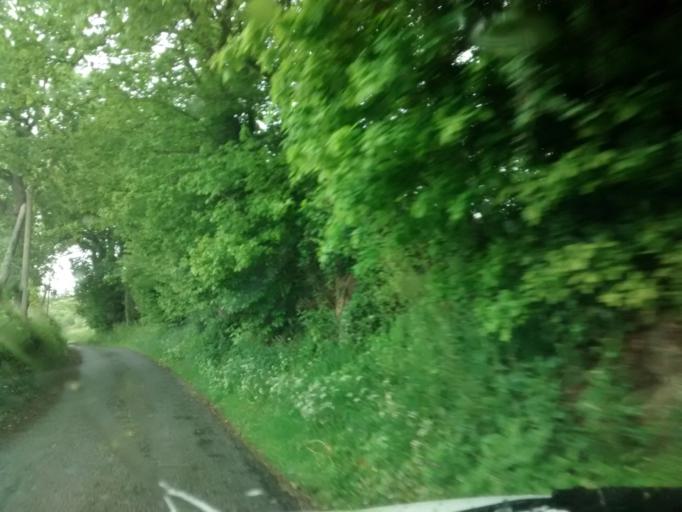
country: FR
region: Brittany
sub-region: Departement d'Ille-et-Vilaine
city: Acigne
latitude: 48.1125
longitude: -1.5665
